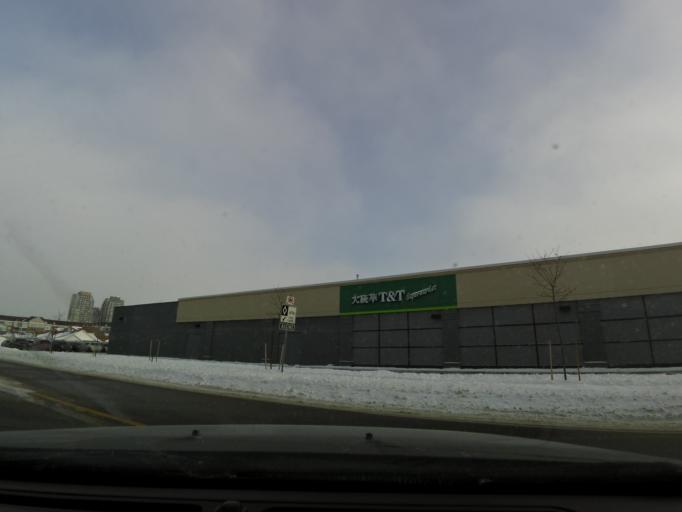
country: CA
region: Ontario
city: Waterloo
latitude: 43.4628
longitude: -80.5389
